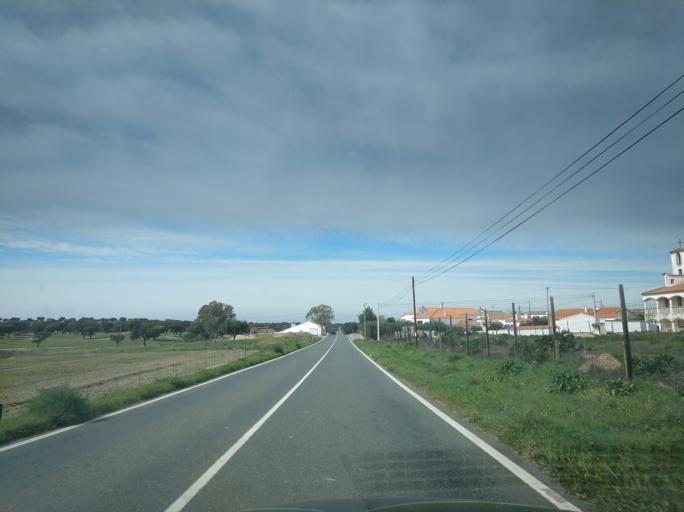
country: PT
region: Beja
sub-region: Mertola
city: Mertola
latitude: 37.7430
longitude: -7.7923
